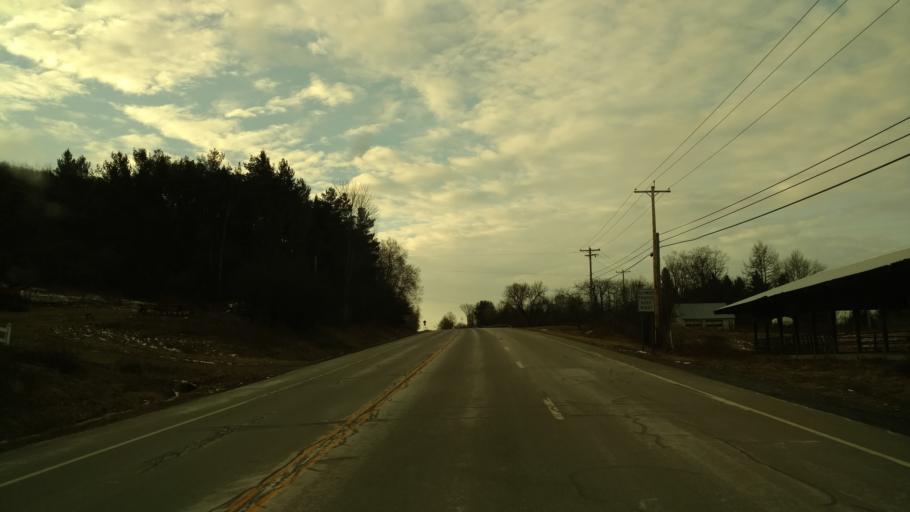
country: US
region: New York
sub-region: Allegany County
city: Wellsville
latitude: 42.0775
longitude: -77.9207
